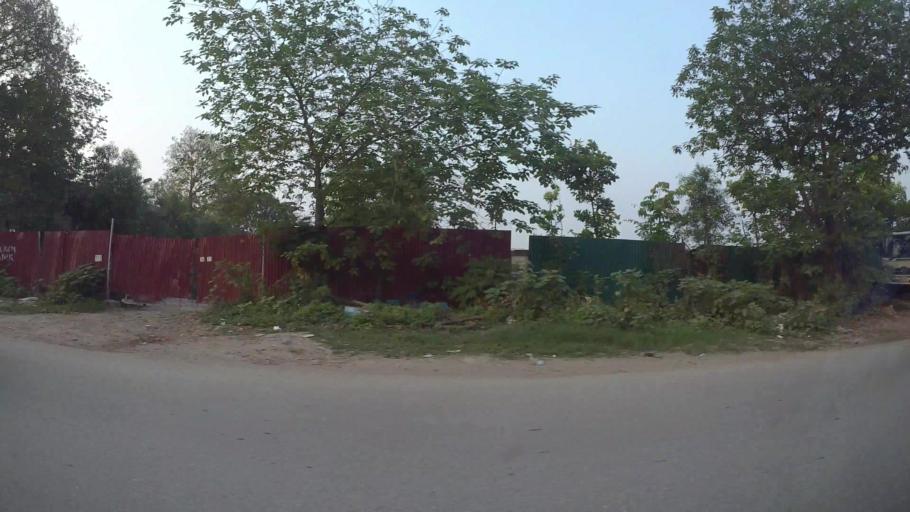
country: VN
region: Ha Noi
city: Tay Ho
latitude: 21.0744
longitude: 105.7985
